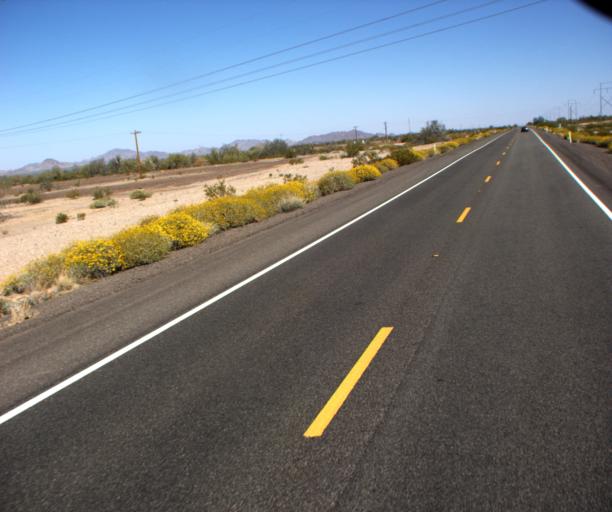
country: US
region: Arizona
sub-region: La Paz County
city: Quartzsite
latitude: 33.5420
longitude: -114.2170
